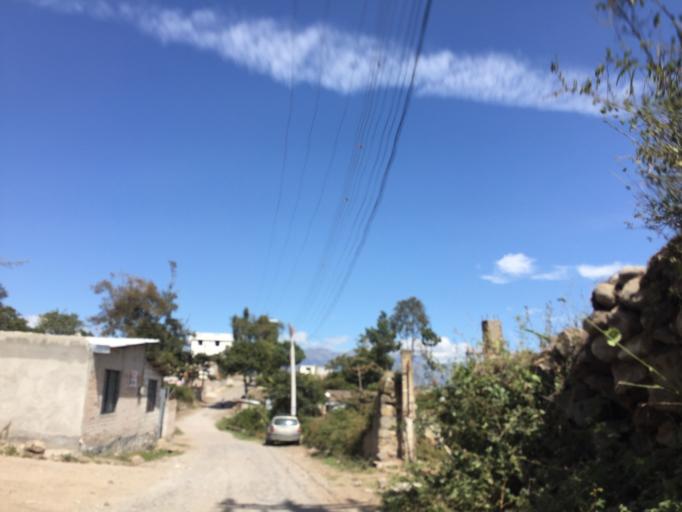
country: EC
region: Imbabura
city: Ibarra
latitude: 0.3138
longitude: -78.1564
